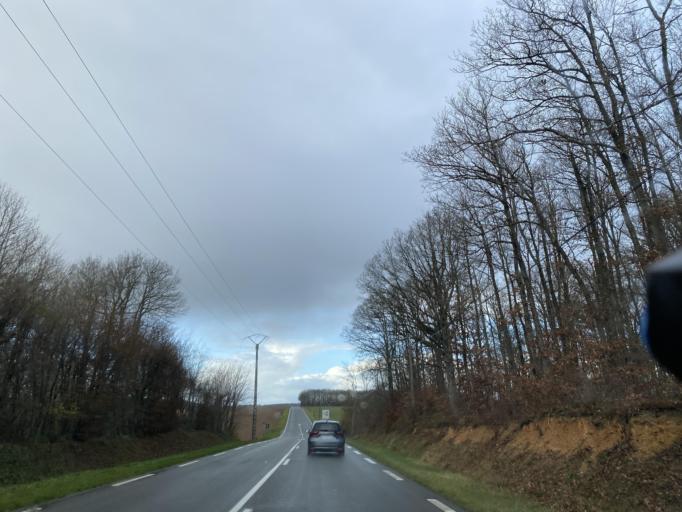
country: FR
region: Centre
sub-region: Departement d'Eure-et-Loir
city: Chateauneuf-en-Thymerais
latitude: 48.5934
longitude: 1.2299
